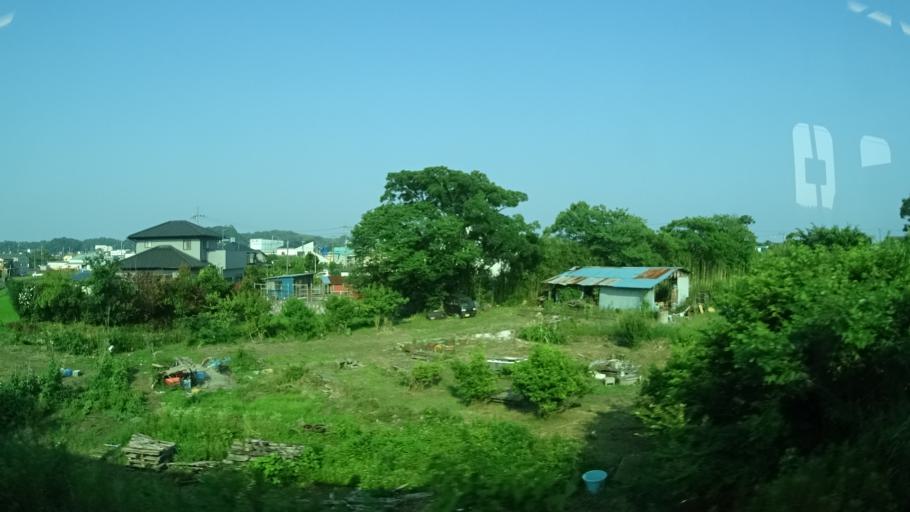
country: JP
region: Ibaraki
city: Kitaibaraki
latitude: 36.8310
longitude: 140.7763
